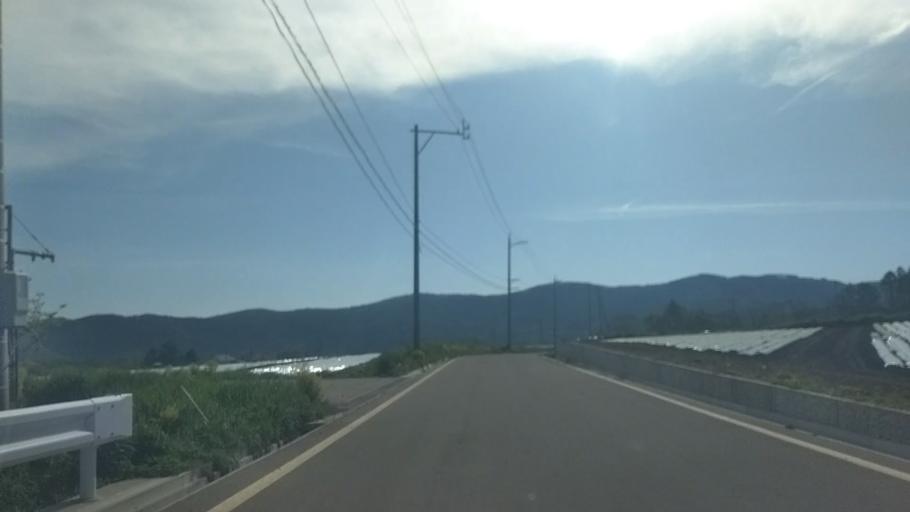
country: JP
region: Yamanashi
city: Nirasaki
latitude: 35.9362
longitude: 138.4728
